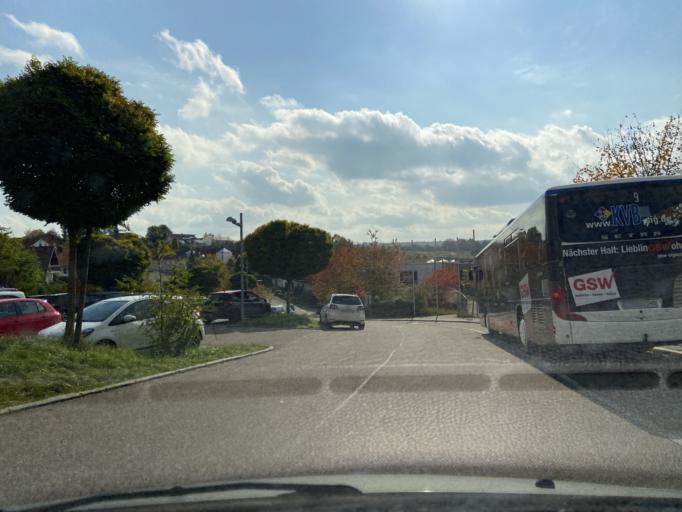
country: DE
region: Baden-Wuerttemberg
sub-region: Tuebingen Region
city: Sigmaringen
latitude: 48.0826
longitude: 9.2124
